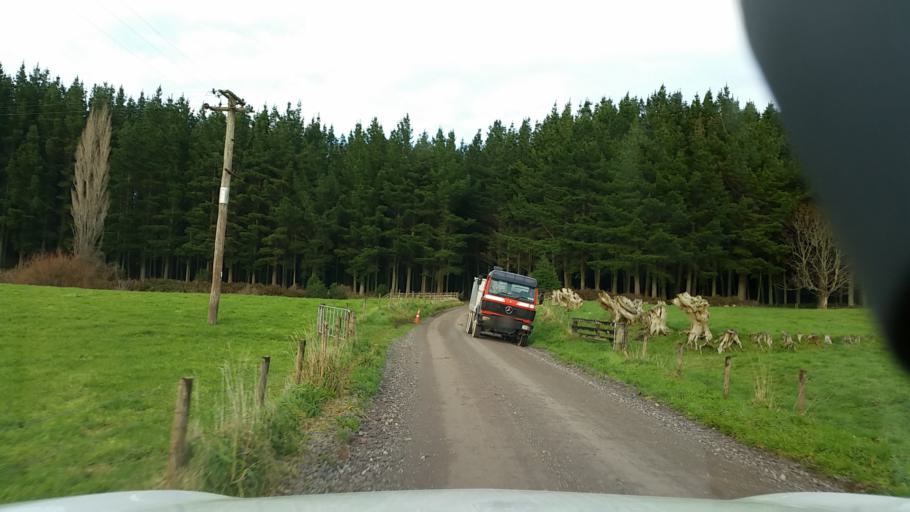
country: NZ
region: Bay of Plenty
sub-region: Rotorua District
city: Rotorua
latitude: -38.2323
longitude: 176.1581
